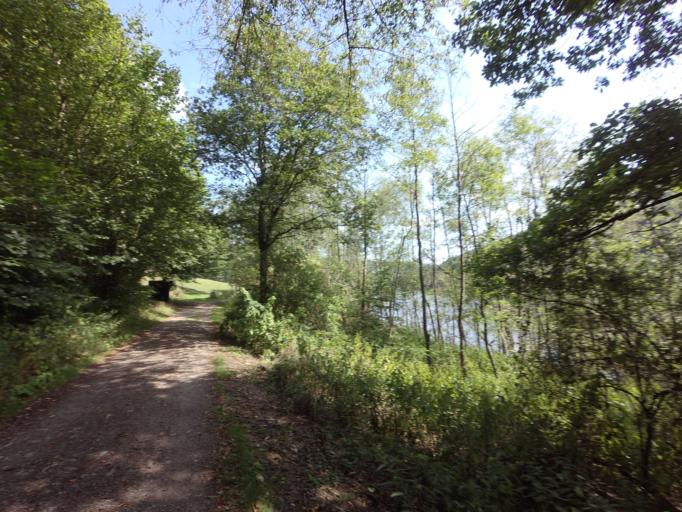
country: DE
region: North Rhine-Westphalia
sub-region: Regierungsbezirk Koln
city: Simmerath
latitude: 50.5962
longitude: 6.3799
